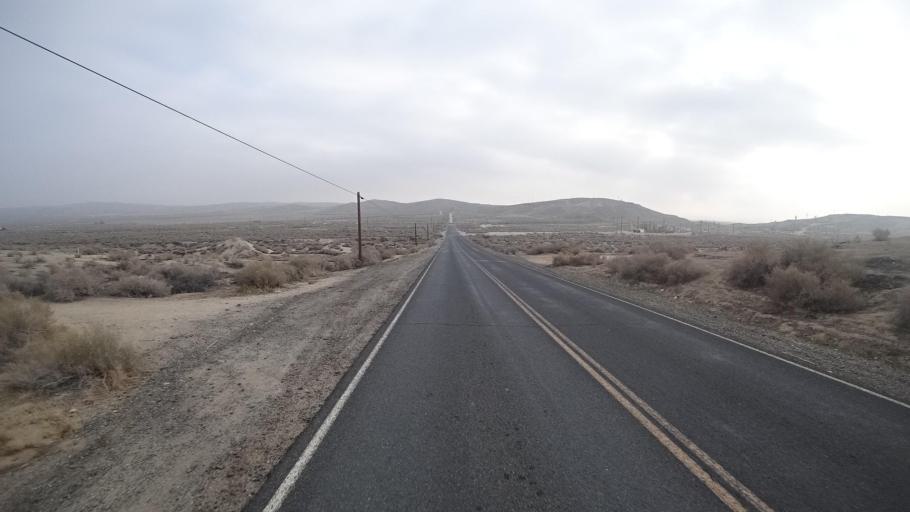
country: US
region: California
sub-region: Kern County
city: Ford City
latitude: 35.1907
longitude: -119.4457
